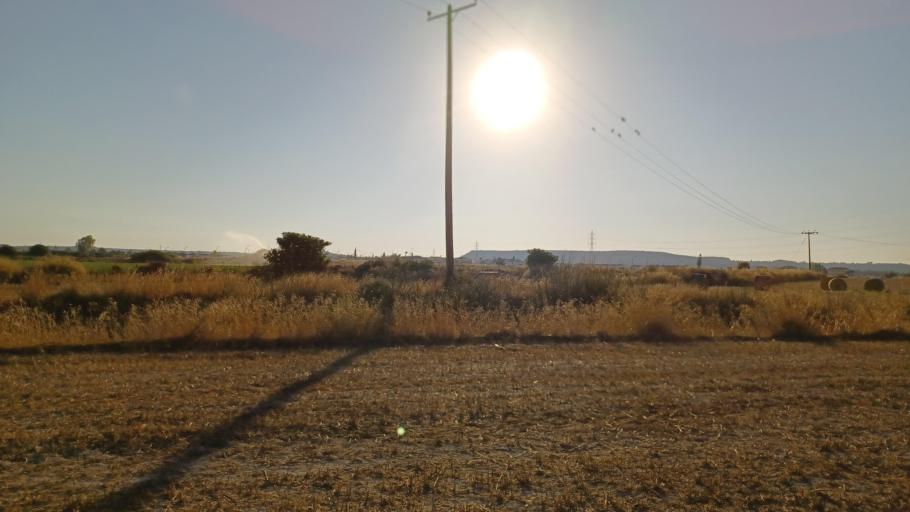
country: CY
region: Larnaka
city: Voroklini
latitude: 34.9888
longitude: 33.6740
